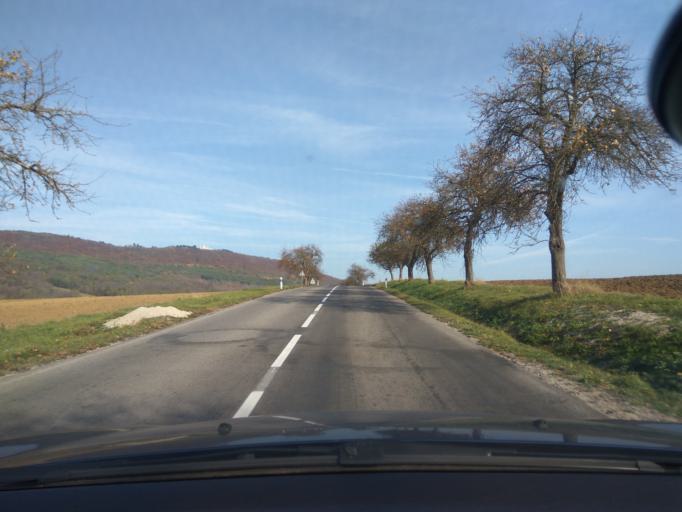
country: SK
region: Nitriansky
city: Brezova pod Bradlom
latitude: 48.6657
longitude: 17.5477
